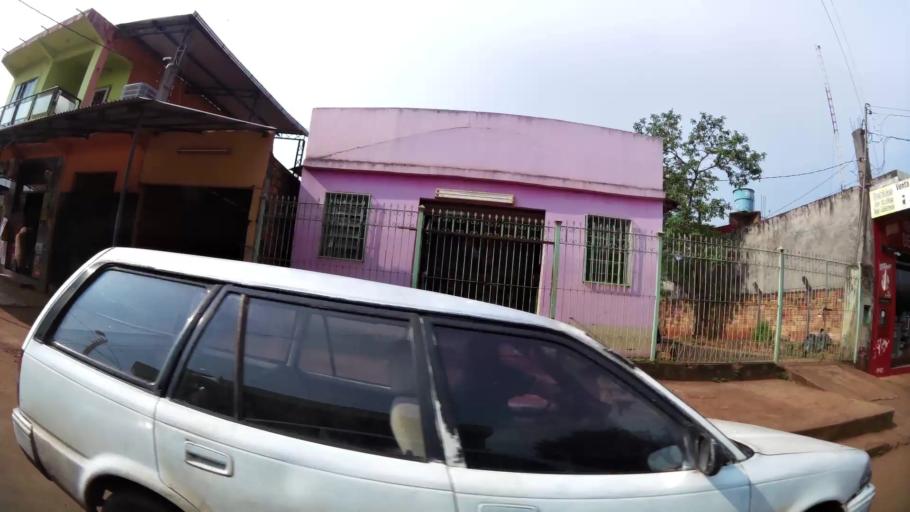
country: PY
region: Alto Parana
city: Ciudad del Este
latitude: -25.4818
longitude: -54.6547
